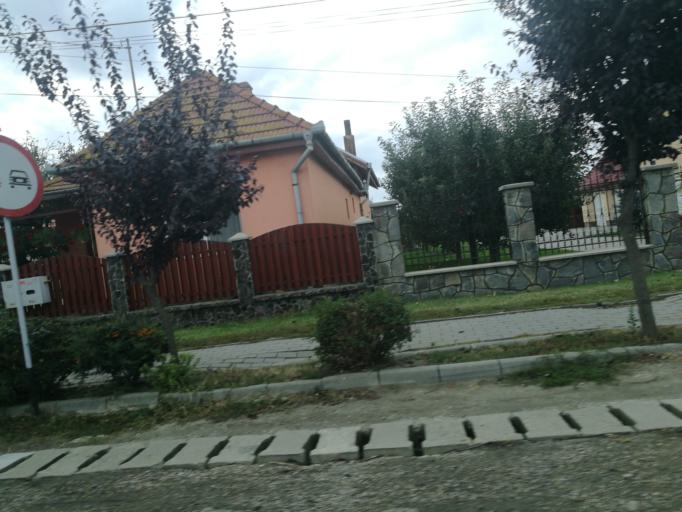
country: RO
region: Mures
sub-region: Comuna Ungheni
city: Ungheni
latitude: 46.4868
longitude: 24.4611
